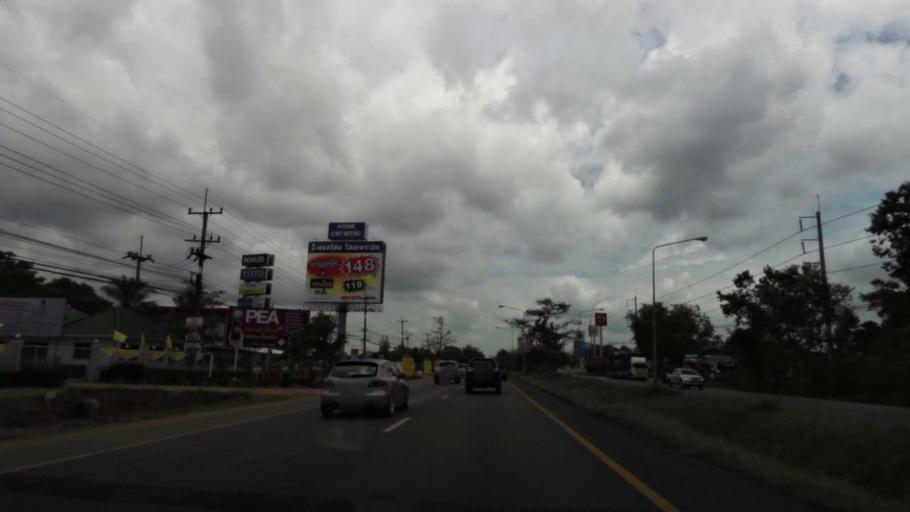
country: TH
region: Rayong
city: Klaeng
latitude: 12.7835
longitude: 101.6876
